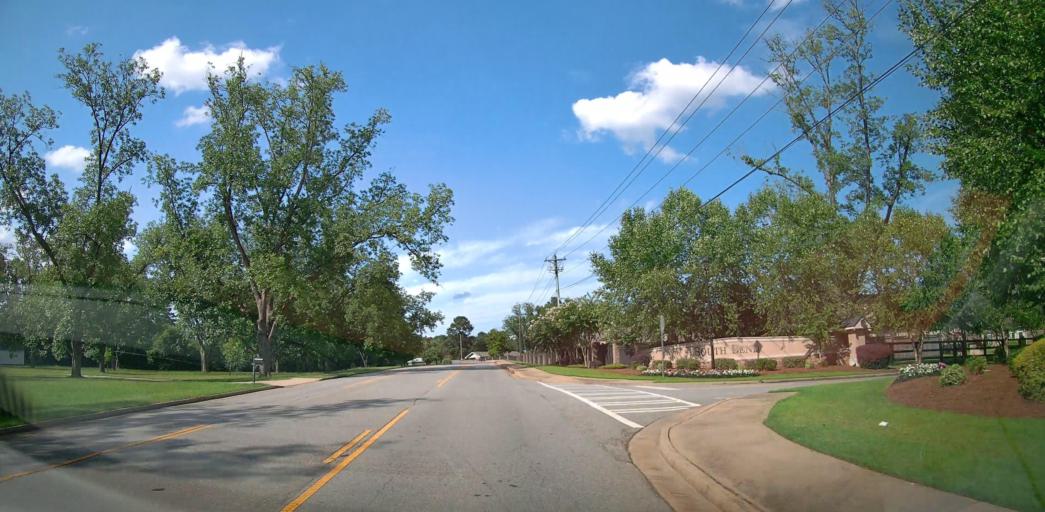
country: US
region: Georgia
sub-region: Houston County
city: Robins Air Force Base
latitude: 32.5342
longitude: -83.6055
